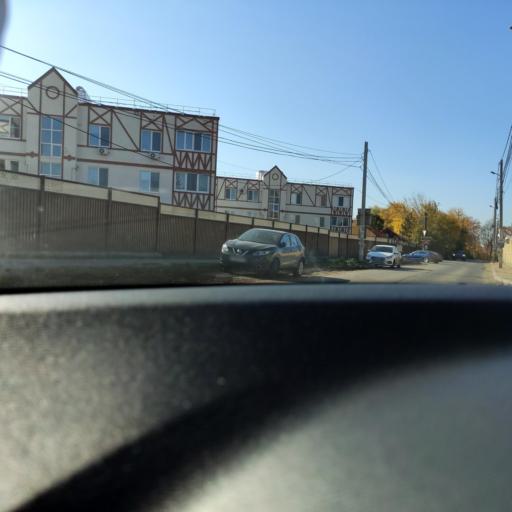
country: RU
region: Samara
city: Samara
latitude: 53.2684
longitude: 50.1981
